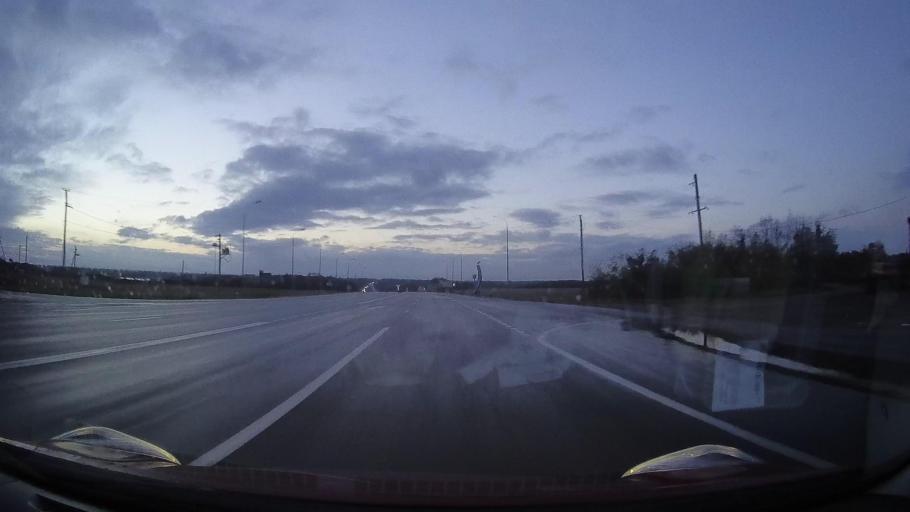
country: RU
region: Krasnodarskiy
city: Zavetnyy
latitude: 44.9101
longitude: 41.1647
